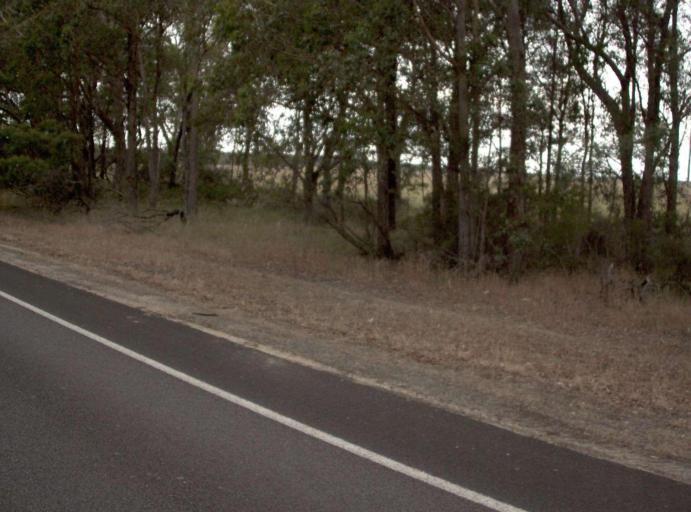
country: AU
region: Victoria
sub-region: Wellington
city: Sale
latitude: -38.5102
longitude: 146.8886
